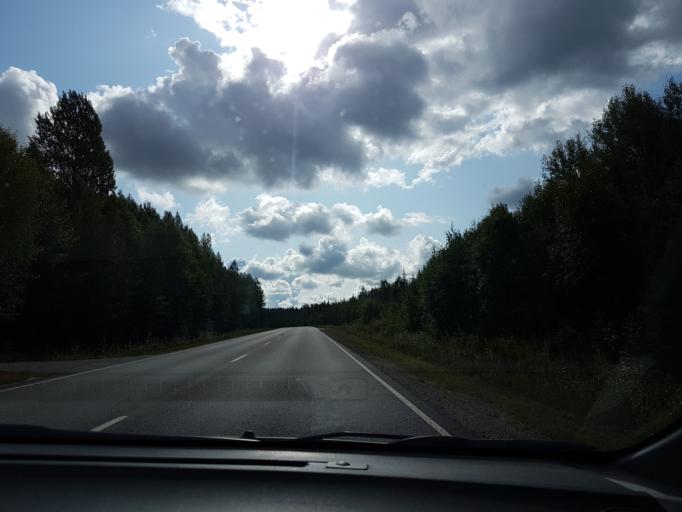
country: FI
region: Uusimaa
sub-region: Helsinki
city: Sibbo
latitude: 60.4722
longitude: 25.2377
